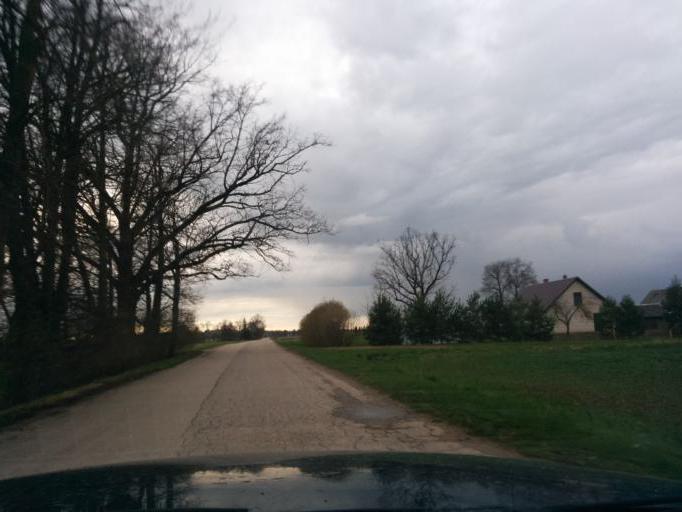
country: LT
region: Siauliu apskritis
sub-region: Joniskis
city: Joniskis
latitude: 56.3744
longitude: 23.5462
